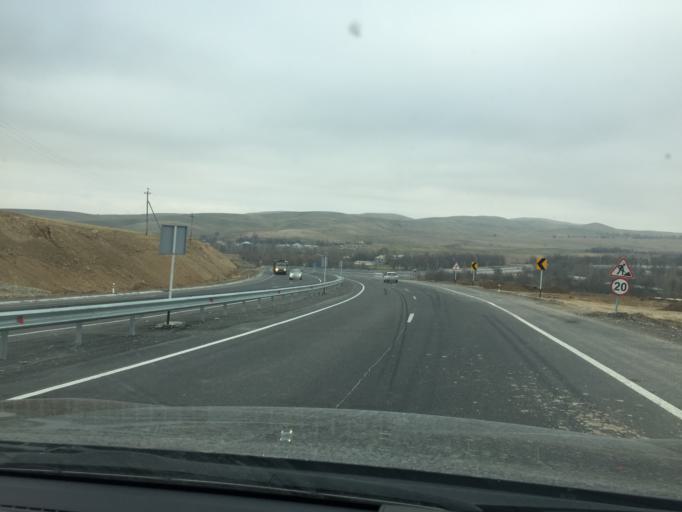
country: KZ
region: Ongtustik Qazaqstan
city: Sastobe
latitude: 42.4949
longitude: 69.9598
